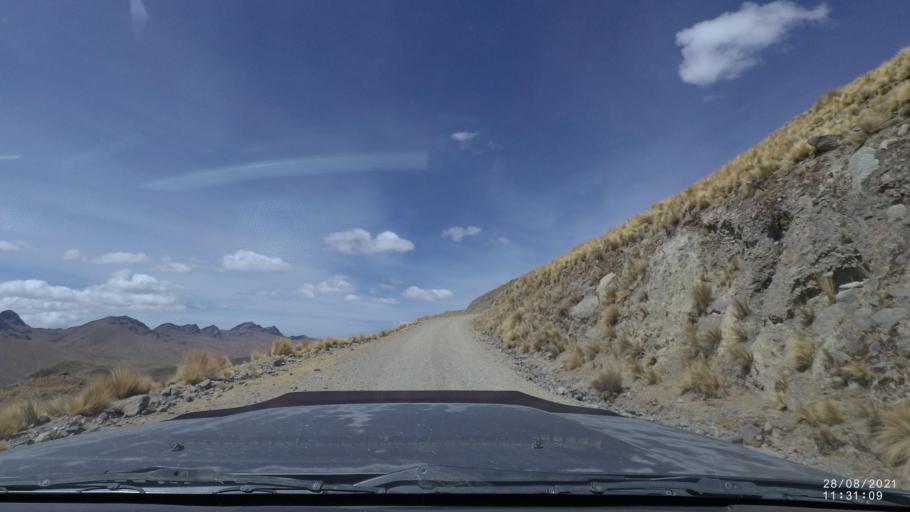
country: BO
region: Cochabamba
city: Sipe Sipe
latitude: -17.1810
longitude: -66.3661
